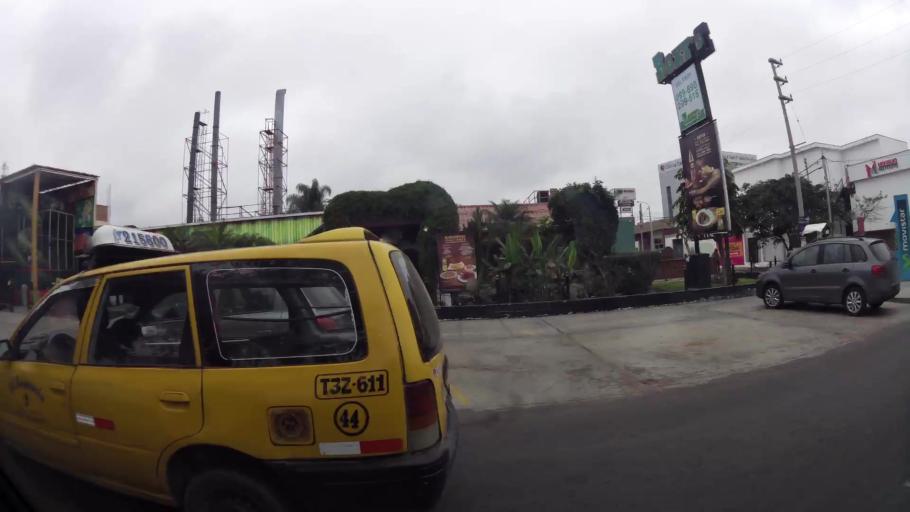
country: PE
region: La Libertad
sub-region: Provincia de Trujillo
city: Trujillo
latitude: -8.1201
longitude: -79.0348
